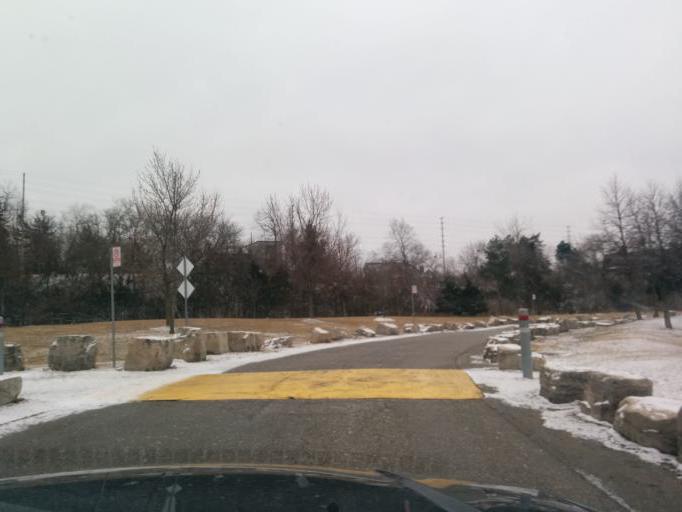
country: CA
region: Ontario
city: Mississauga
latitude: 43.5462
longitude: -79.6549
